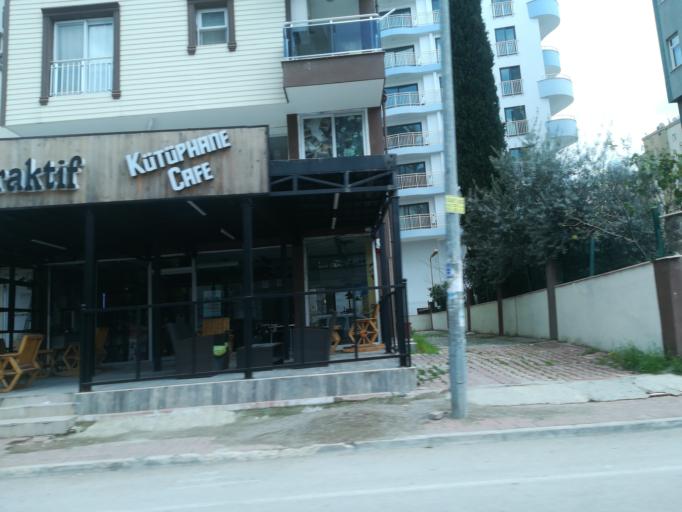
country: TR
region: Adana
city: Adana
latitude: 37.0372
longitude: 35.3127
